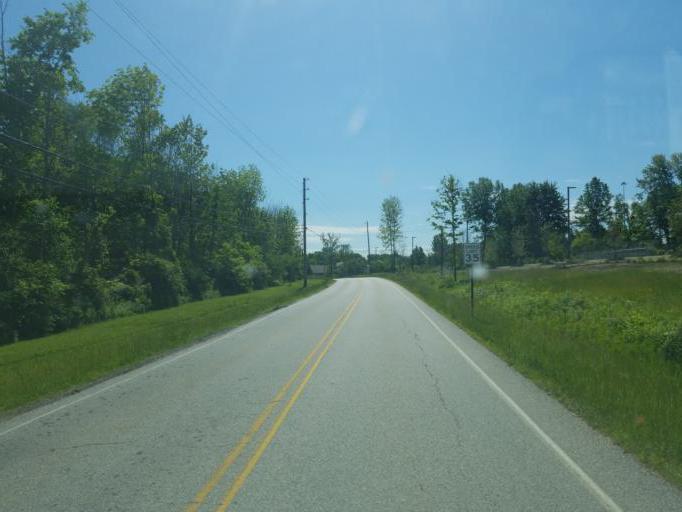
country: US
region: Ohio
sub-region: Summit County
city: Boston Heights
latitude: 41.2607
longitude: -81.4961
